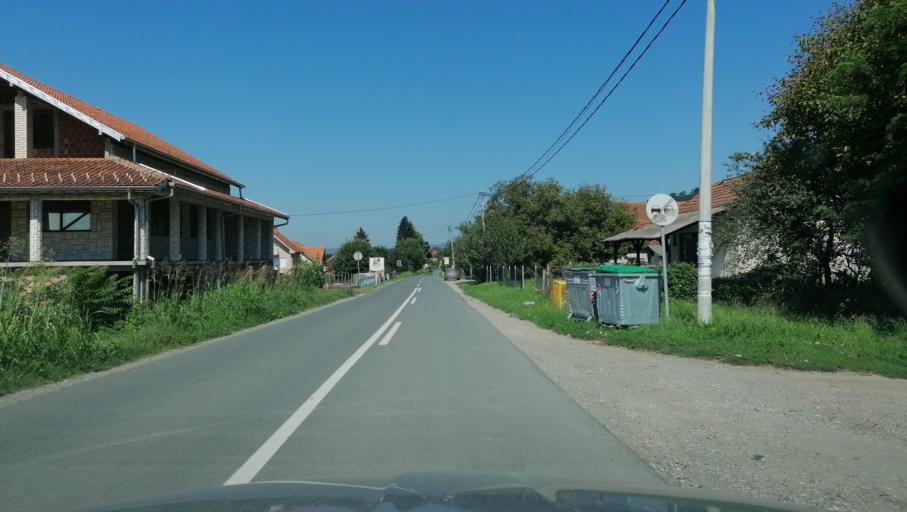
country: RS
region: Central Serbia
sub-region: Raski Okrug
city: Vrnjacka Banja
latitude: 43.6684
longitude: 20.9104
